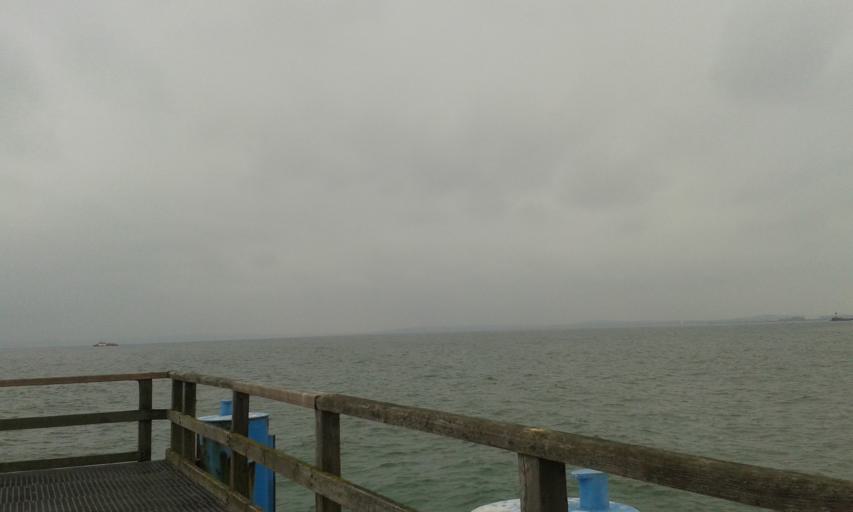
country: DE
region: Mecklenburg-Vorpommern
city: Sassnitz
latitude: 54.5158
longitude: 13.6559
